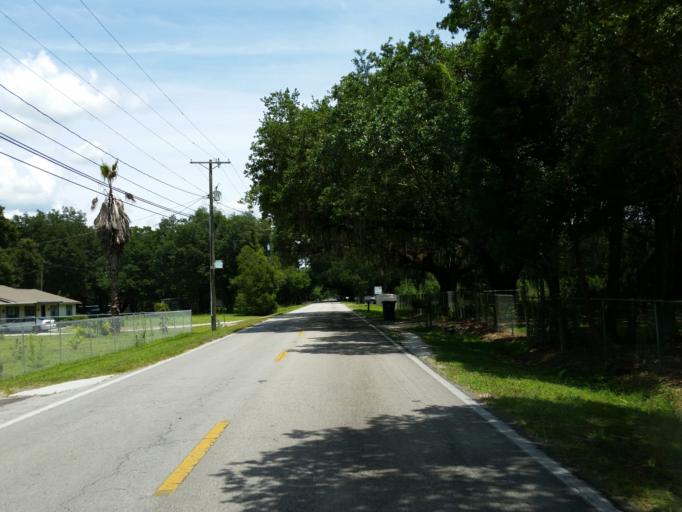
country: US
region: Florida
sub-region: Hillsborough County
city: Dover
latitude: 28.0471
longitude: -82.2136
